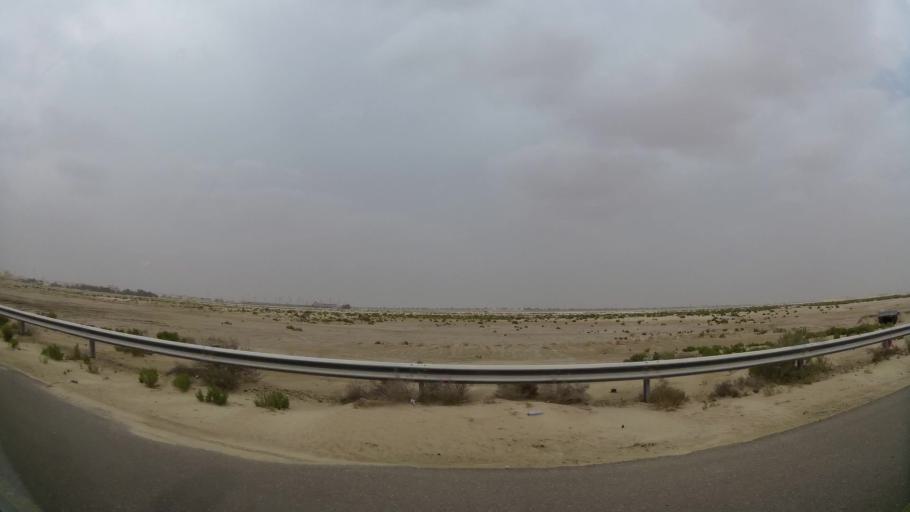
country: AE
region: Abu Dhabi
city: Abu Dhabi
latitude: 24.3809
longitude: 54.6768
